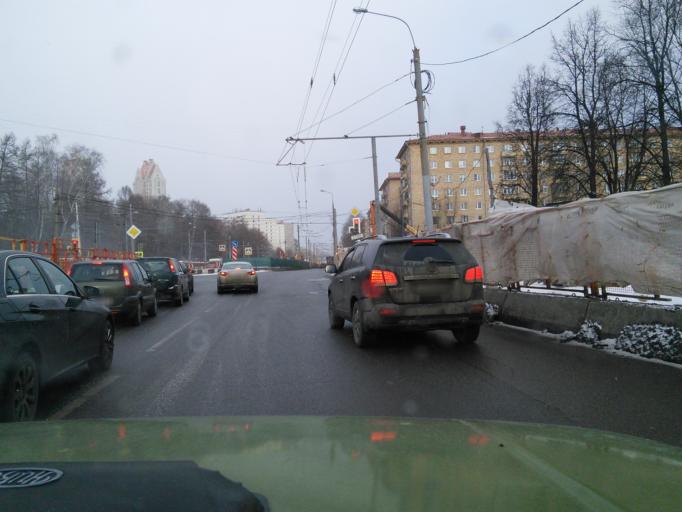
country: RU
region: Moskovskaya
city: Khoroshevo-Mnevniki
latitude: 55.7878
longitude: 37.4844
